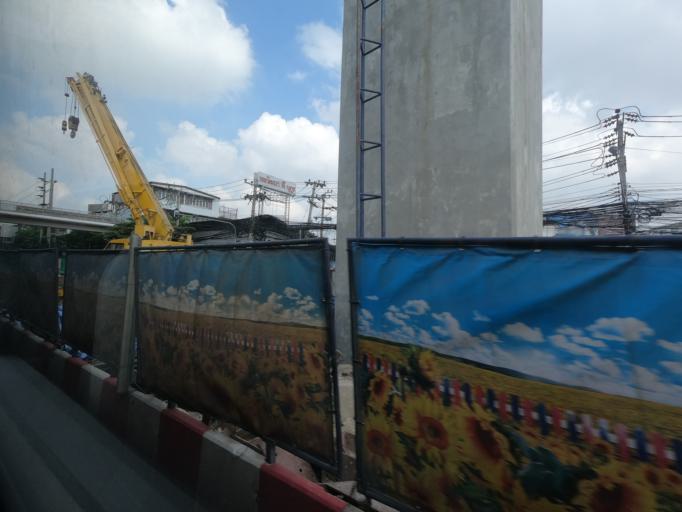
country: TH
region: Bangkok
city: Wang Thonglang
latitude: 13.7869
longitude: 100.6078
